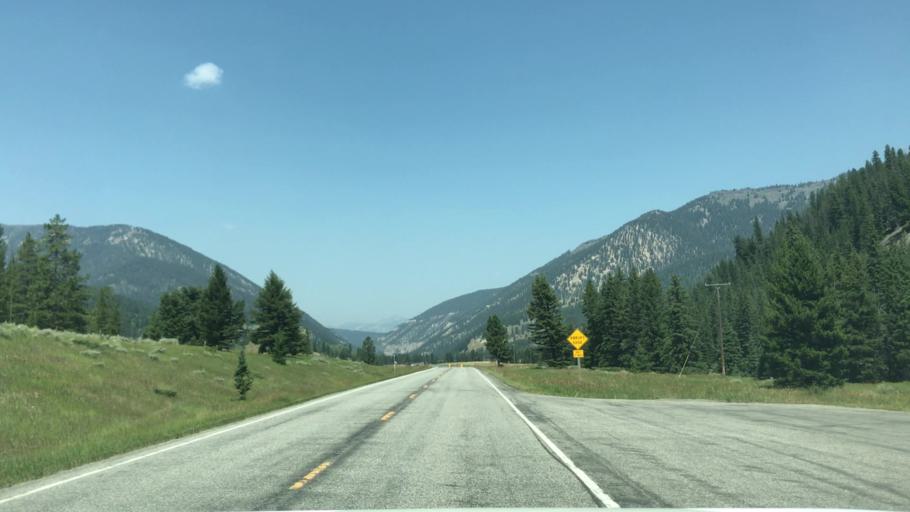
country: US
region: Montana
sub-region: Gallatin County
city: Big Sky
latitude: 45.0908
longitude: -111.2136
